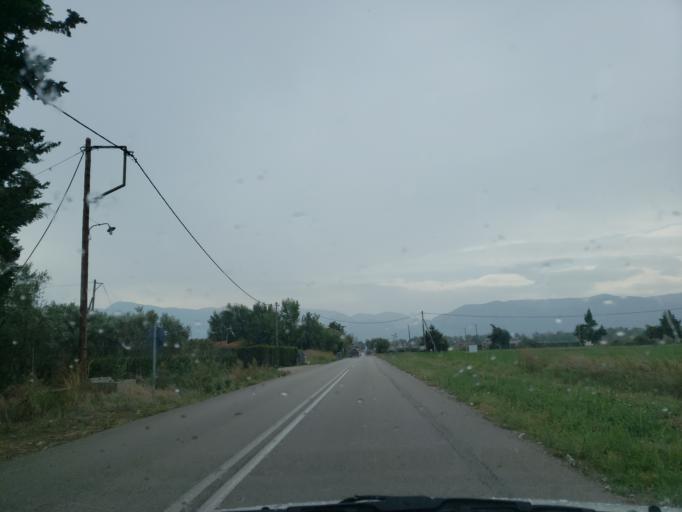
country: GR
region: Central Greece
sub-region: Nomos Fthiotidos
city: Rodhitsa
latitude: 38.8588
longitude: 22.4401
